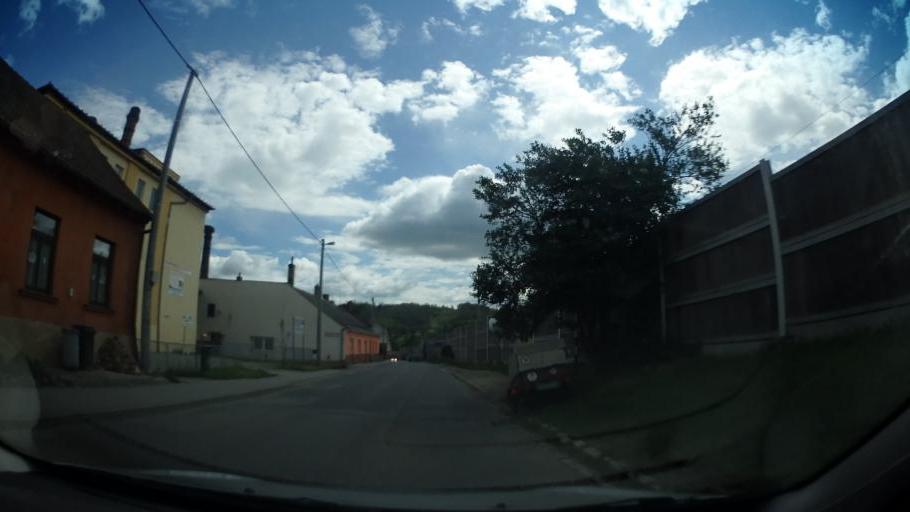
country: CZ
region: South Moravian
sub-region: Okres Blansko
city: Letovice
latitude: 49.5491
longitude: 16.5722
